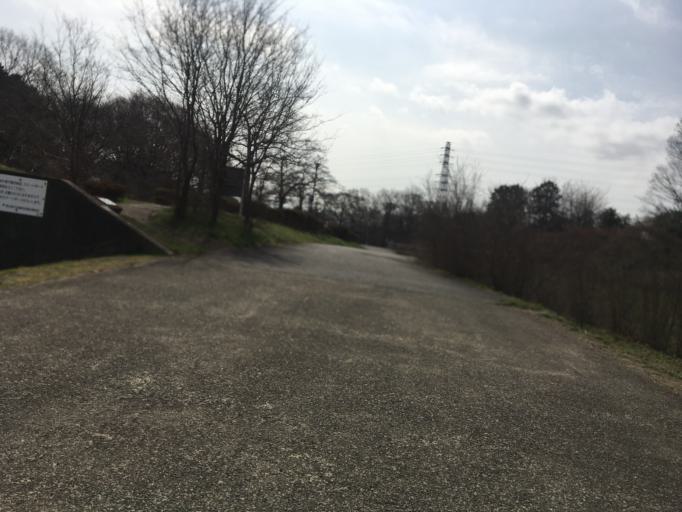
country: JP
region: Tokyo
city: Kamirenjaku
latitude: 35.6912
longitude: 139.5190
